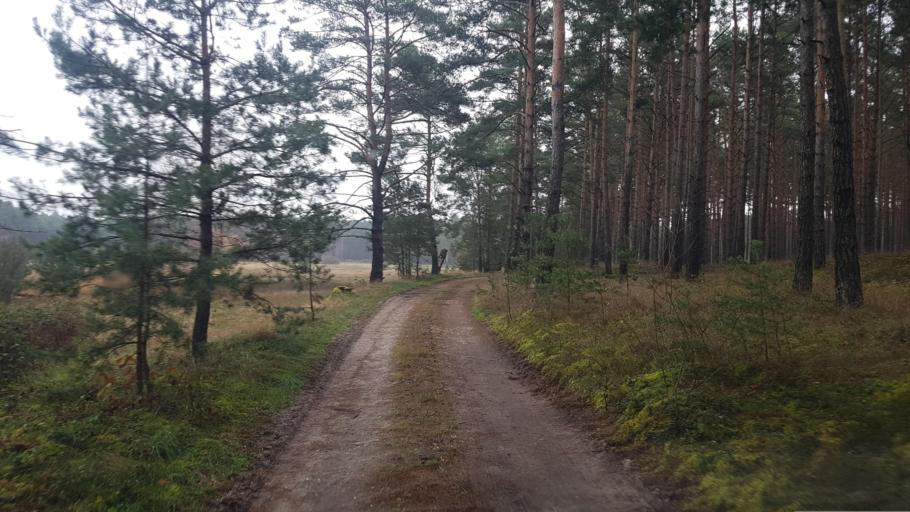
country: DE
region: Brandenburg
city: Sallgast
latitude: 51.6483
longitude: 13.8313
